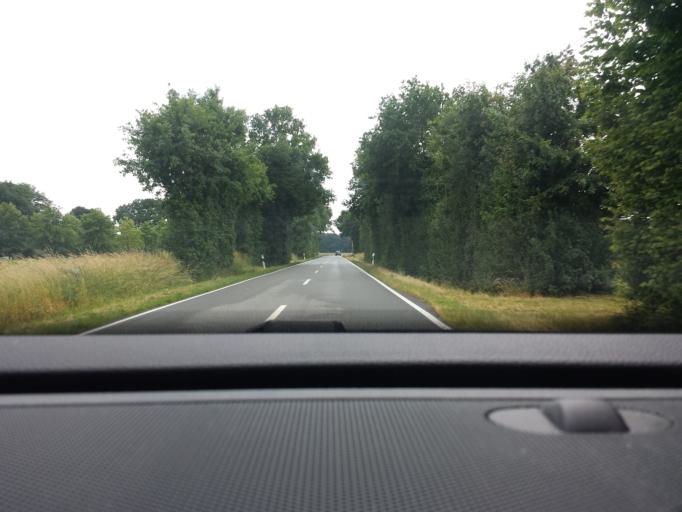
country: NL
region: Gelderland
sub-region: Berkelland
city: Eibergen
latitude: 52.0575
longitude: 6.7047
